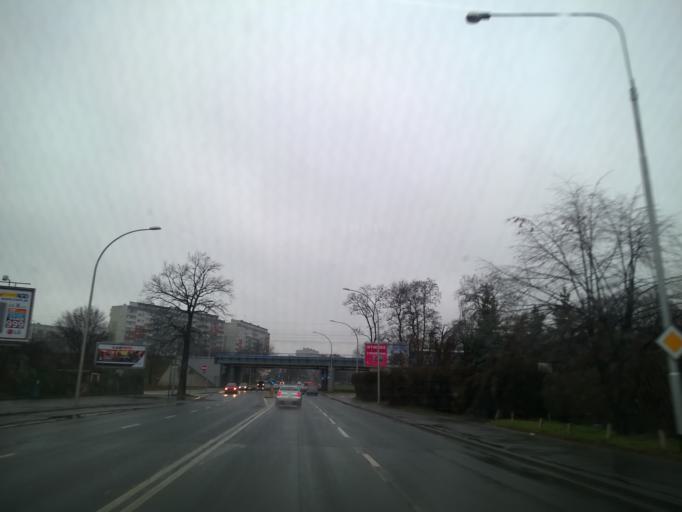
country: PL
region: Lower Silesian Voivodeship
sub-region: Powiat wroclawski
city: Wroclaw
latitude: 51.1260
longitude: 17.0026
